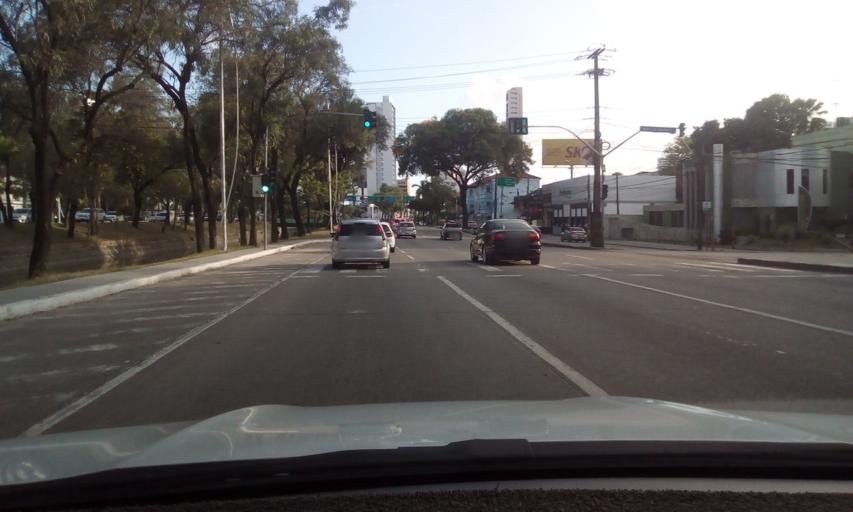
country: BR
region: Pernambuco
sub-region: Recife
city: Recife
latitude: -8.0571
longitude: -34.8981
